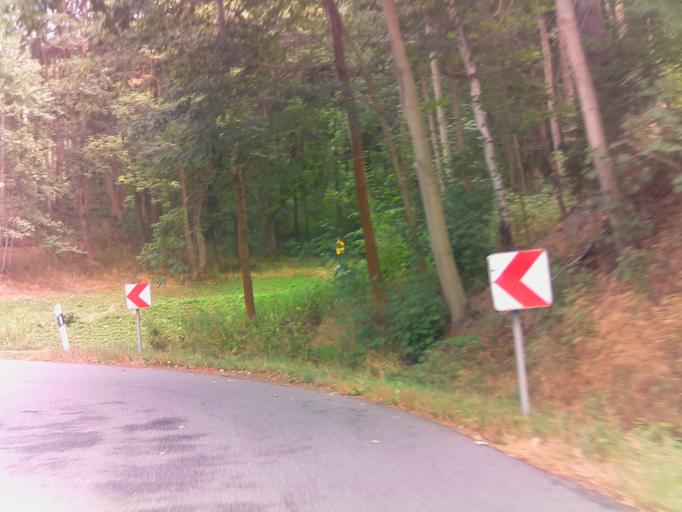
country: DE
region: Thuringia
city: Remptendorf
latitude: 50.5310
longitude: 11.6727
